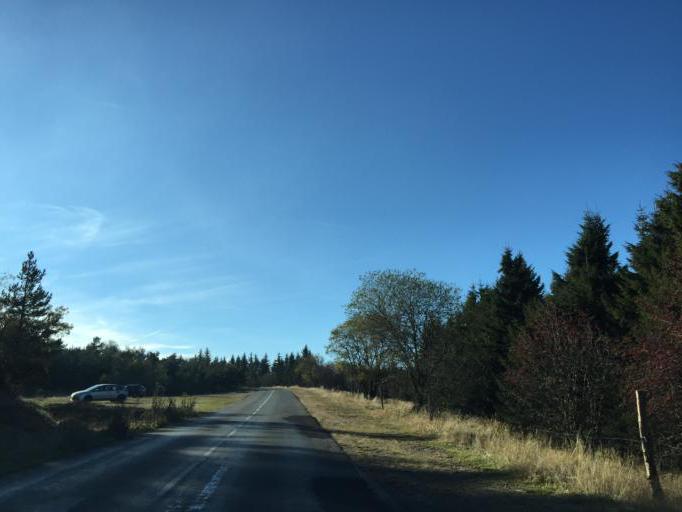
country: FR
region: Rhone-Alpes
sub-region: Departement de la Loire
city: Saint-Julien-Molin-Molette
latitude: 45.3861
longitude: 4.5725
